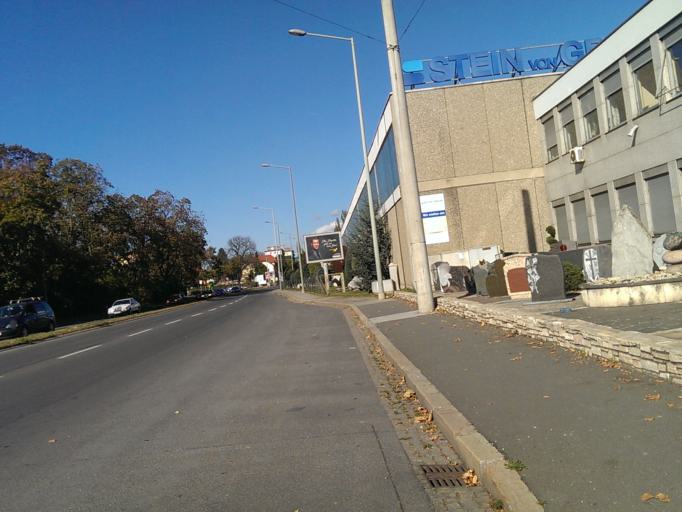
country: AT
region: Styria
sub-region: Graz Stadt
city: Graz
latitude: 47.0457
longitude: 15.4301
